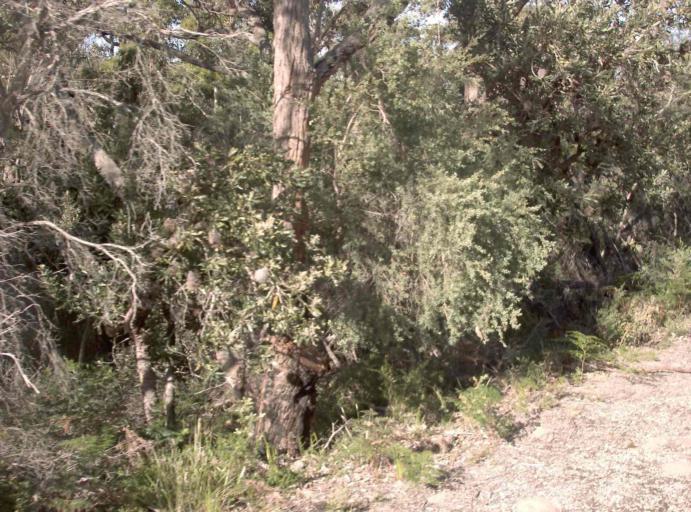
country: AU
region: Victoria
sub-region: East Gippsland
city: Lakes Entrance
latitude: -37.7976
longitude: 148.6997
